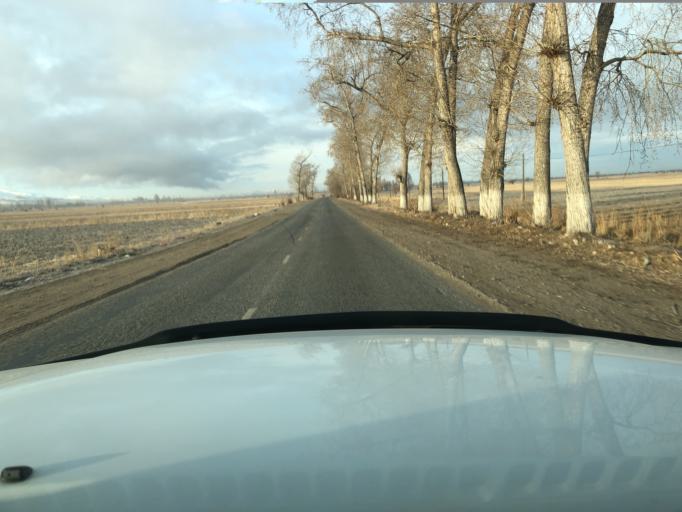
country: KG
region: Ysyk-Koel
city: Karakol
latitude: 42.4763
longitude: 78.3233
